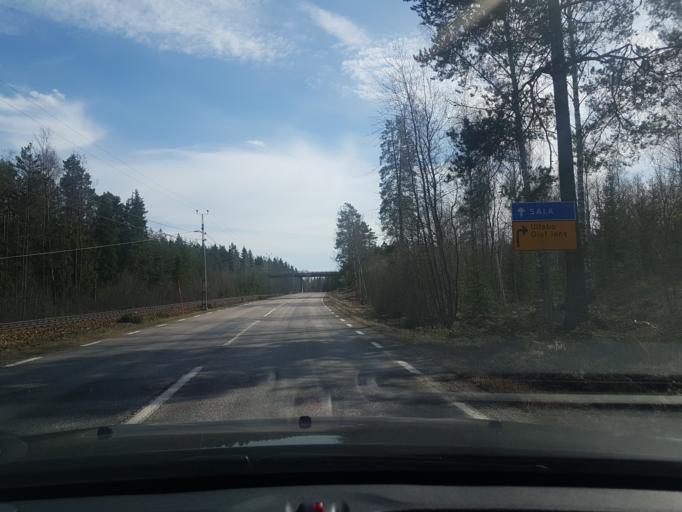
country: SE
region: Vaestmanland
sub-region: Sala Kommun
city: Sala
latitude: 59.9706
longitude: 16.5030
